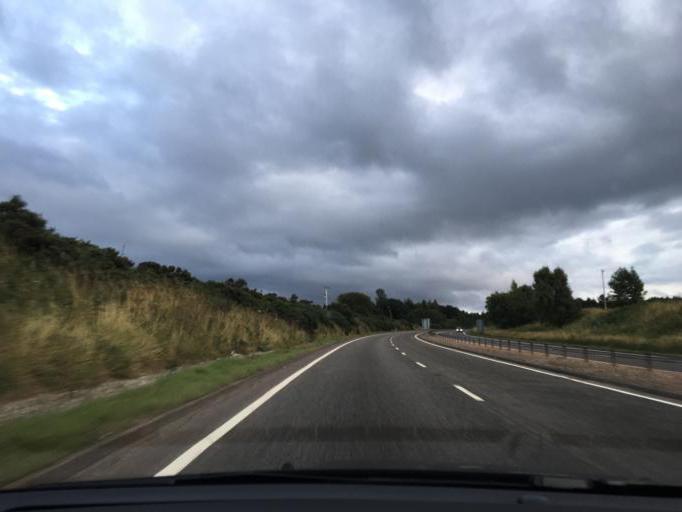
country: GB
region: Scotland
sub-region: Highland
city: Inverness
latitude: 57.4626
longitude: -4.1694
